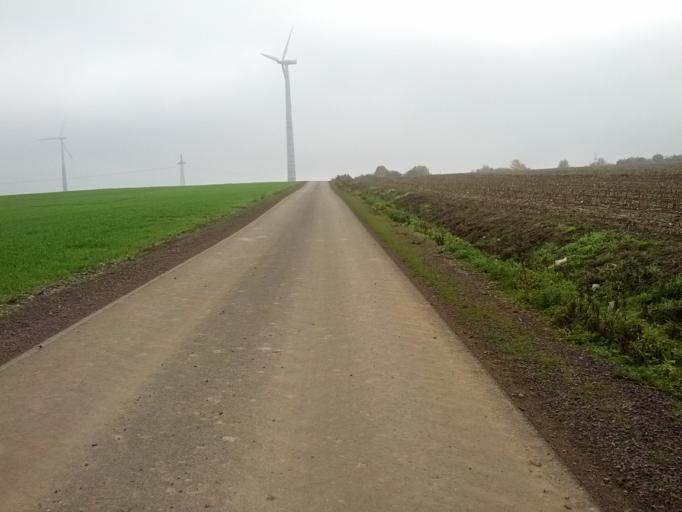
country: DE
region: Thuringia
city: Bischofroda
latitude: 51.0046
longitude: 10.3911
